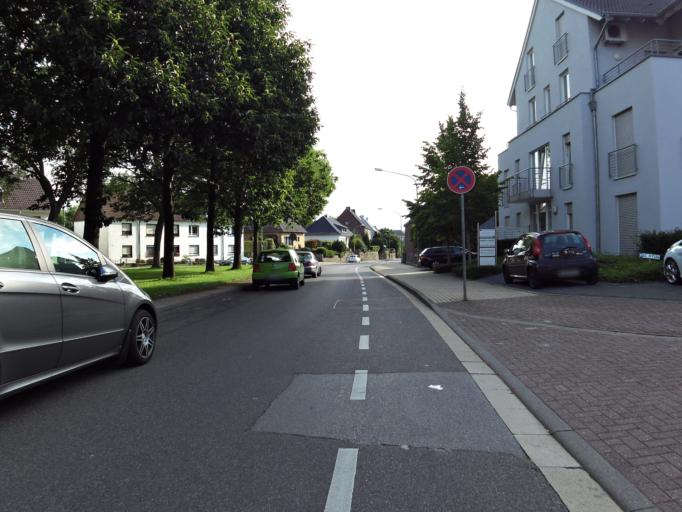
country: DE
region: North Rhine-Westphalia
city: Baesweiler
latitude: 50.9102
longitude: 6.1749
